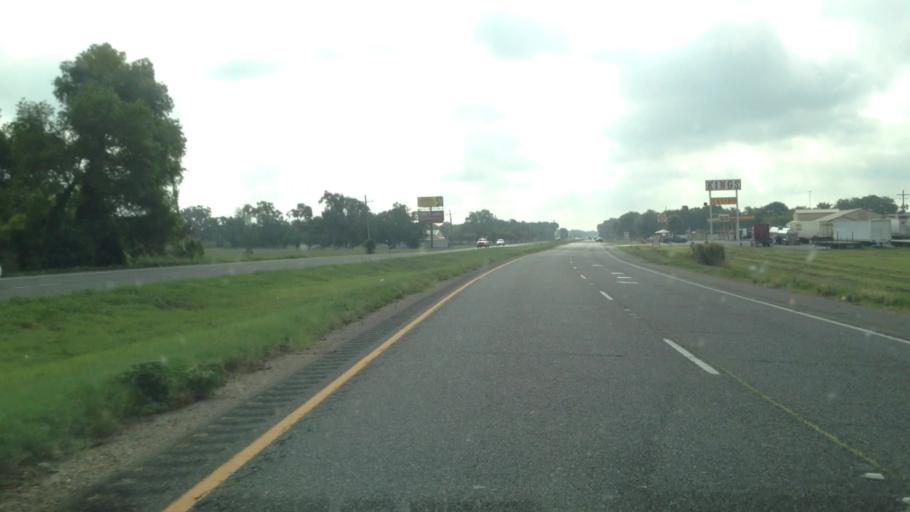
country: US
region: Louisiana
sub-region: Saint Landry Parish
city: Port Barre
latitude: 30.5476
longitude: -92.0039
